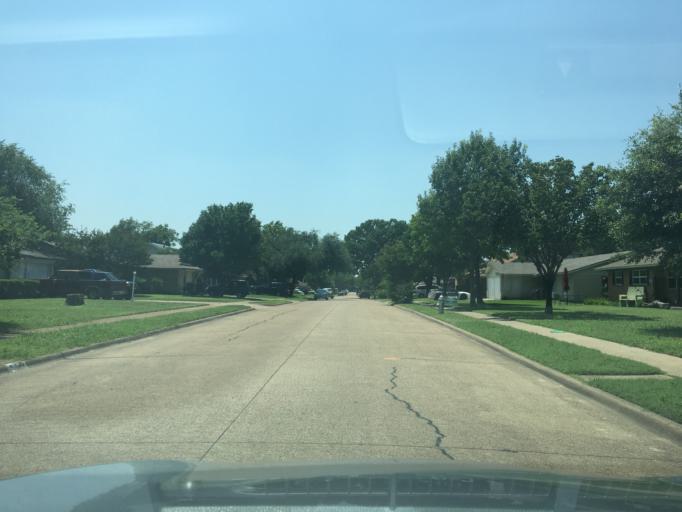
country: US
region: Texas
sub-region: Dallas County
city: Richardson
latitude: 32.9183
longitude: -96.7009
